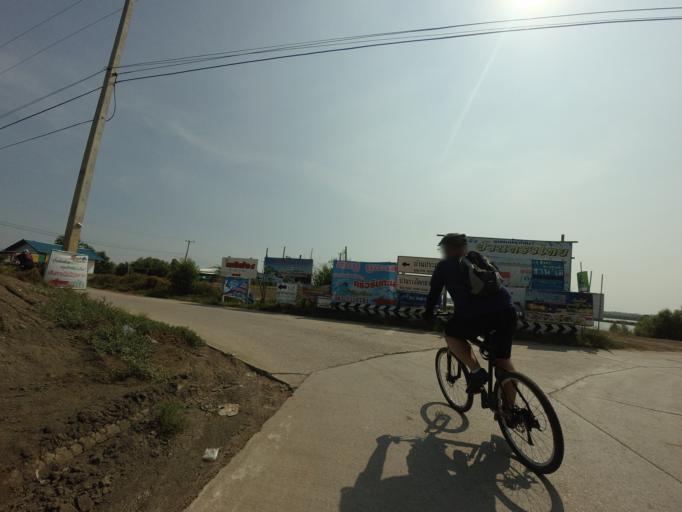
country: TH
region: Samut Sakhon
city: Samut Sakhon
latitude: 13.5002
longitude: 100.3857
